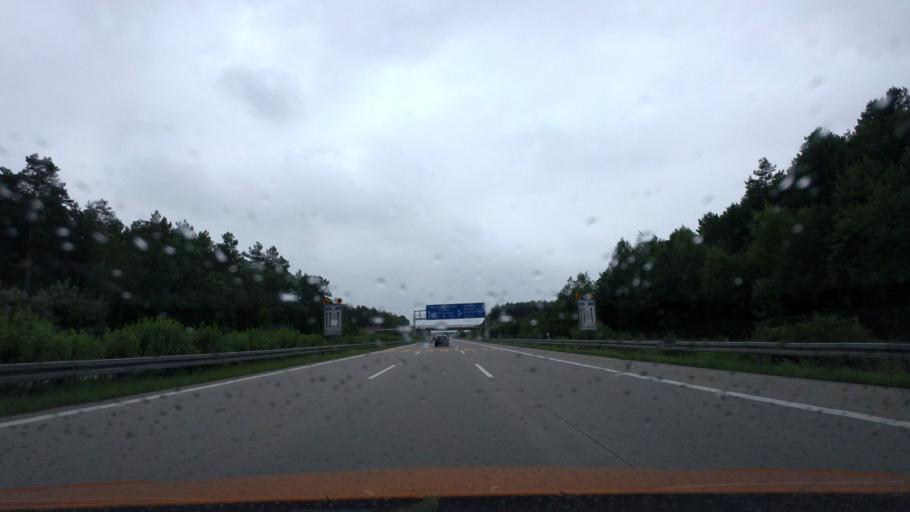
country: DE
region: Brandenburg
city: Erkner
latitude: 52.3385
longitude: 13.7535
